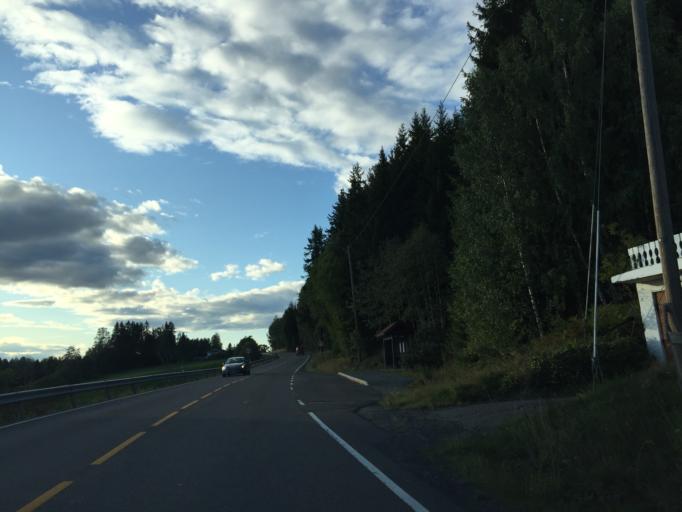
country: NO
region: Akershus
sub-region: Fet
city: Fetsund
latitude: 59.8856
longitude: 11.2064
